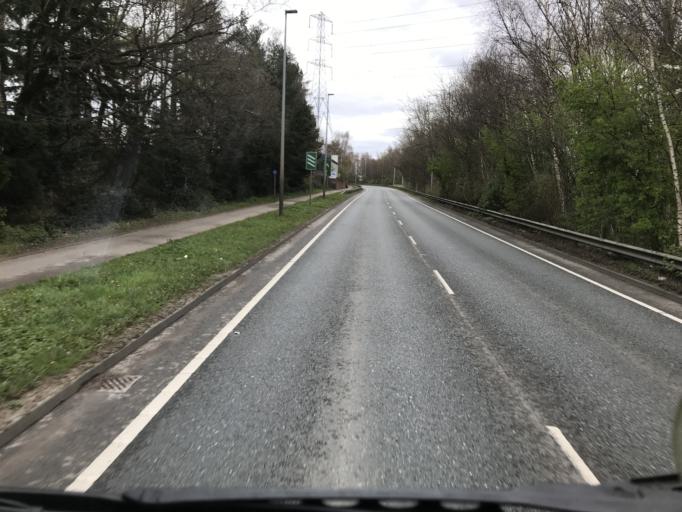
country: GB
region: England
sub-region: City and Borough of Salford
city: Irlam
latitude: 53.4543
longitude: -2.4031
